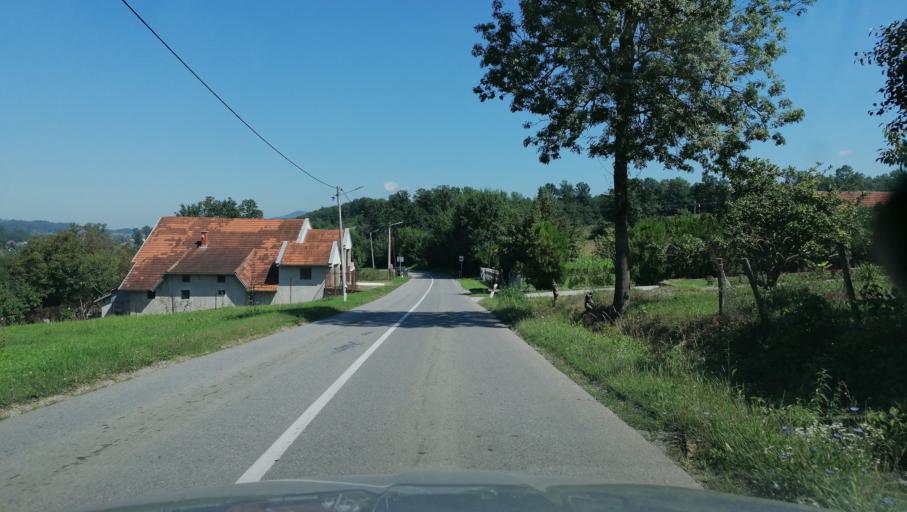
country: RS
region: Central Serbia
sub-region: Raski Okrug
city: Kraljevo
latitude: 43.7195
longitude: 20.8054
